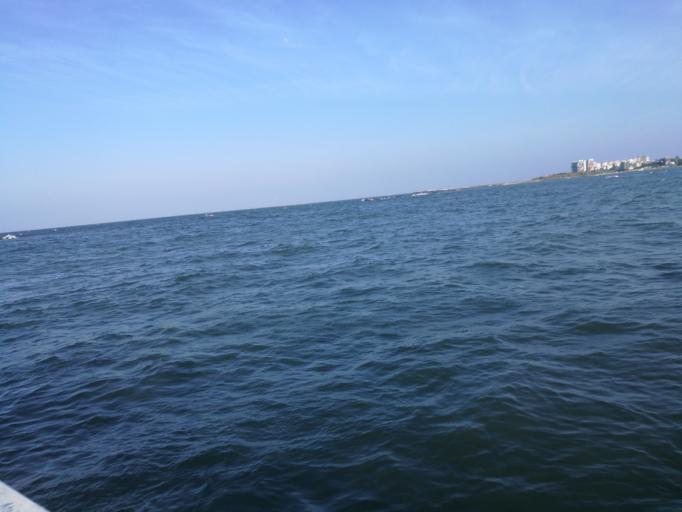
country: RO
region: Constanta
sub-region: Municipiul Constanta
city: Palazu Mare
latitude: 44.2312
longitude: 28.6317
